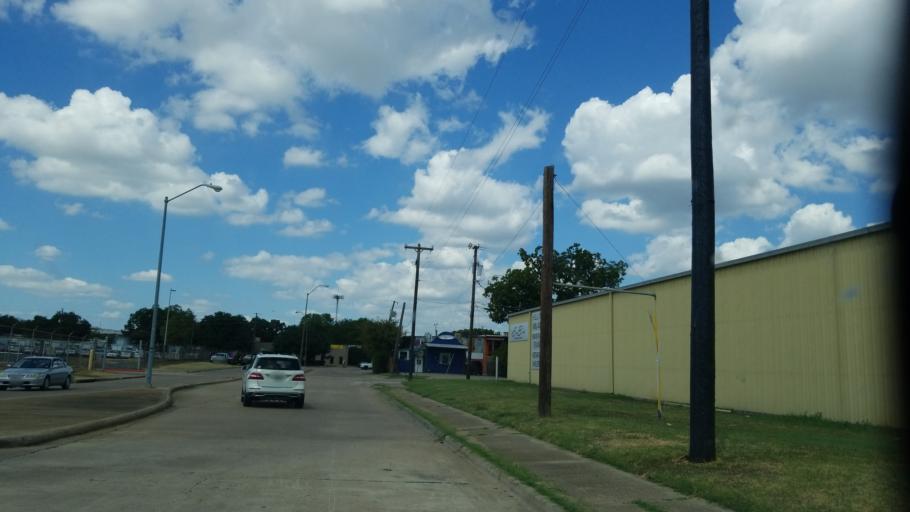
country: US
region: Texas
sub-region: Dallas County
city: Dallas
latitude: 32.7694
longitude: -96.8269
